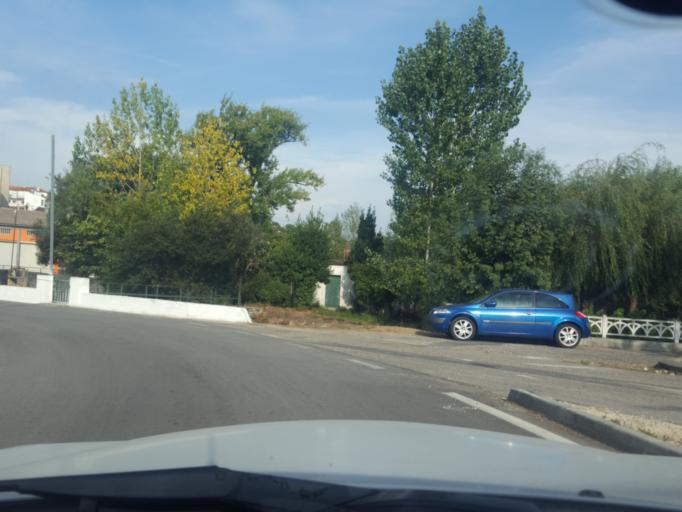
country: PT
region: Leiria
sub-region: Leiria
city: Leiria
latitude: 39.6995
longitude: -8.7886
